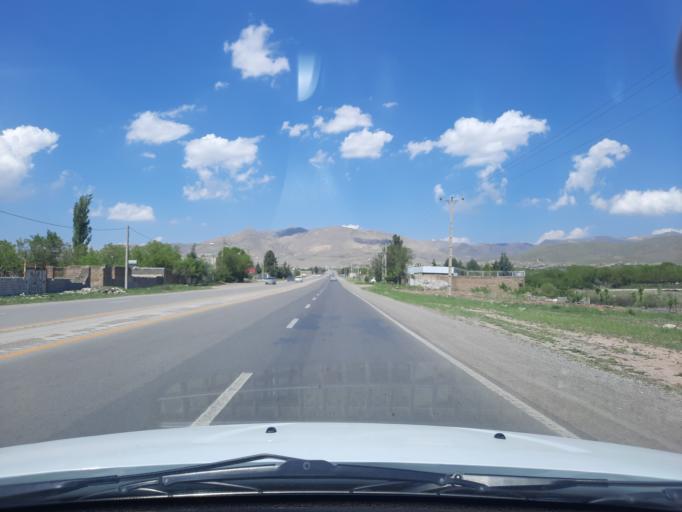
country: IR
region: Qazvin
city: Alvand
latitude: 36.3070
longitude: 50.1446
